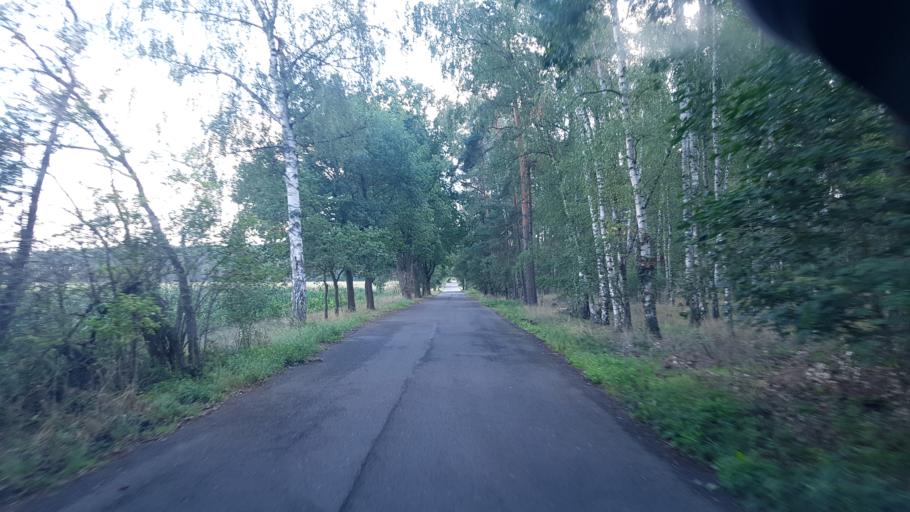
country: DE
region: Brandenburg
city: Drebkau
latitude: 51.6526
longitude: 14.2534
